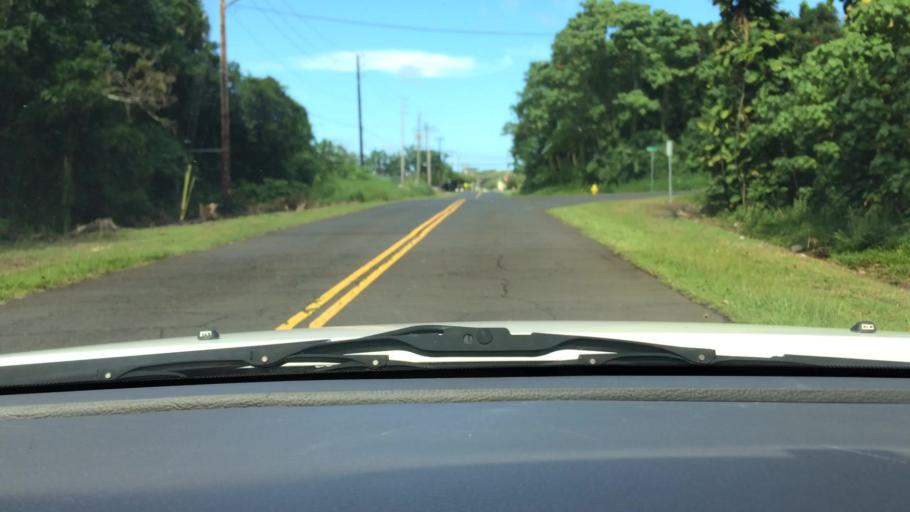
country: US
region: Hawaii
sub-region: Hawaii County
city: Hilo
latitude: 19.7164
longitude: -155.0719
